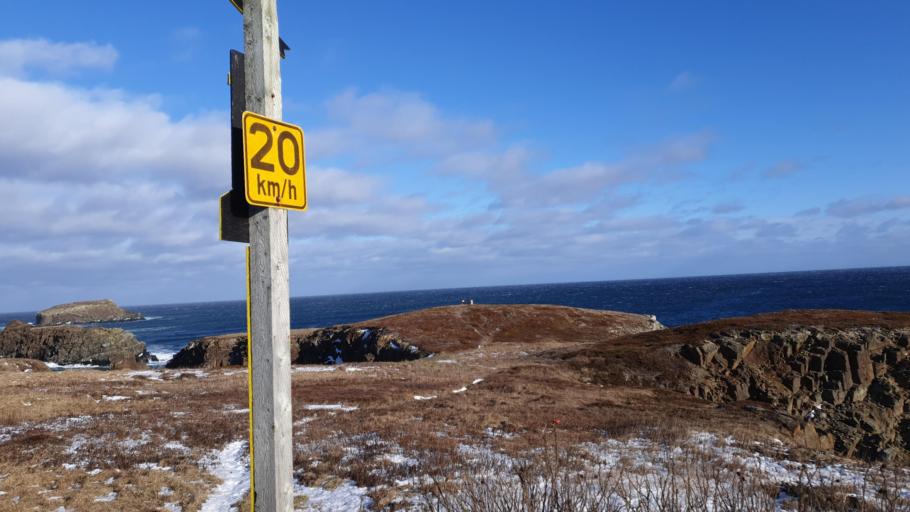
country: CA
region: Newfoundland and Labrador
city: Bonavista
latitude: 48.6255
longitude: -53.0195
